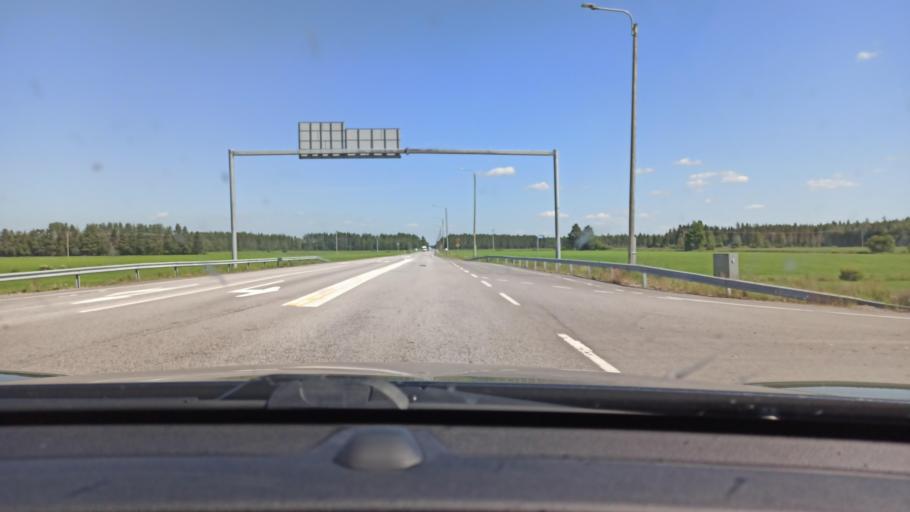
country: FI
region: Northern Ostrobothnia
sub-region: Raahe
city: Ruukki
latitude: 64.7205
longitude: 24.9830
